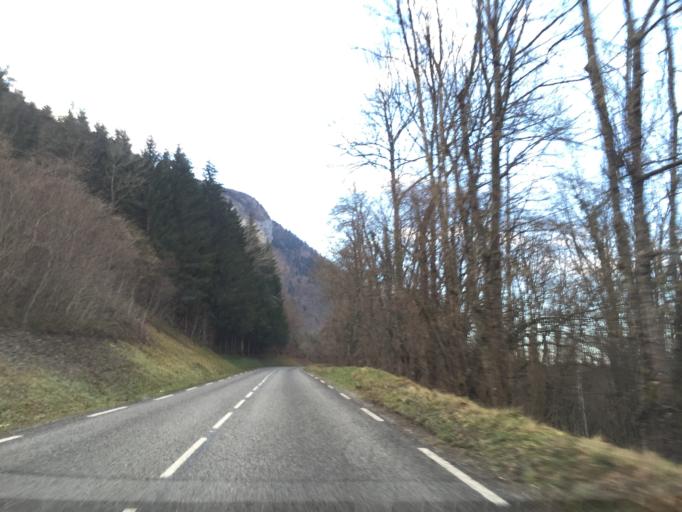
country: FR
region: Rhone-Alpes
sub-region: Departement de la Haute-Savoie
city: Gruffy
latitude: 45.7475
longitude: 6.0762
